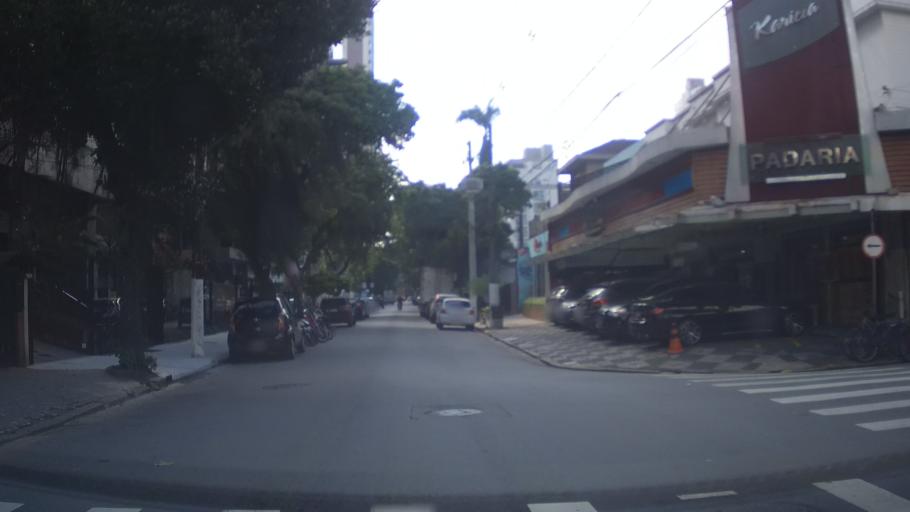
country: BR
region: Sao Paulo
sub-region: Santos
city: Santos
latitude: -23.9681
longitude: -46.3266
